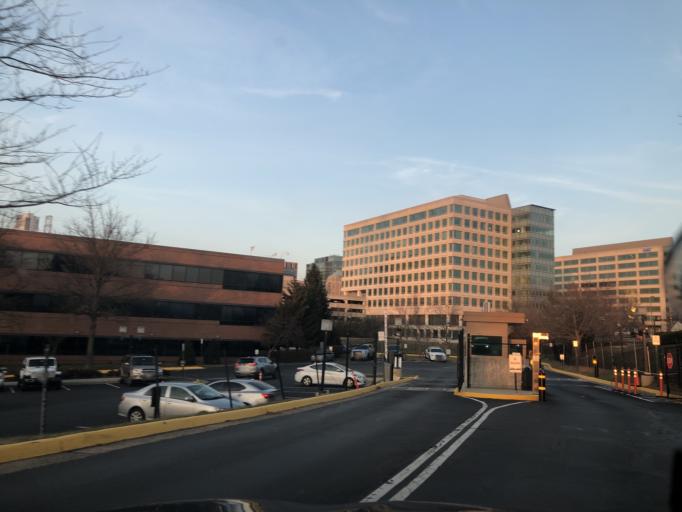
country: US
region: Virginia
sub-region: Fairfax County
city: Reston
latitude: 38.9546
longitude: -77.3592
